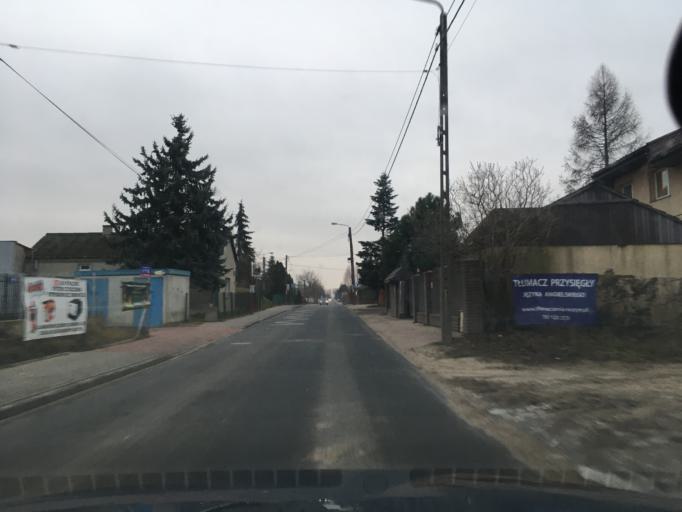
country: PL
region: Masovian Voivodeship
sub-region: Powiat piaseczynski
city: Mysiadlo
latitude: 52.1307
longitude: 20.9799
